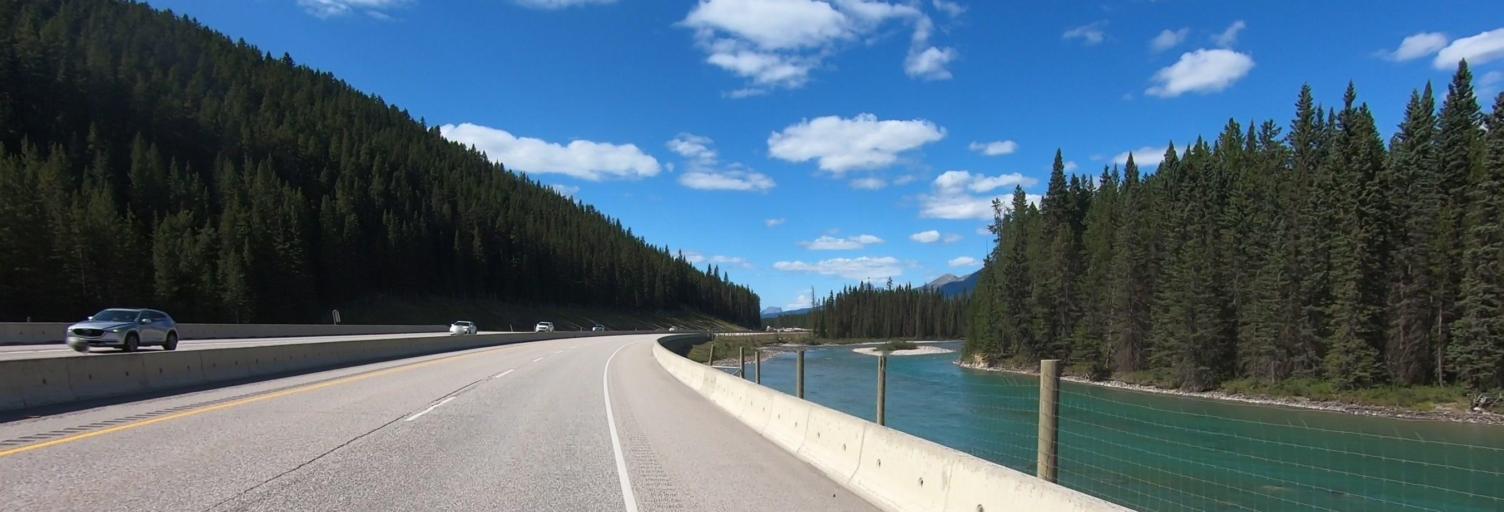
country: CA
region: Alberta
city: Lake Louise
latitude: 51.3280
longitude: -116.0512
